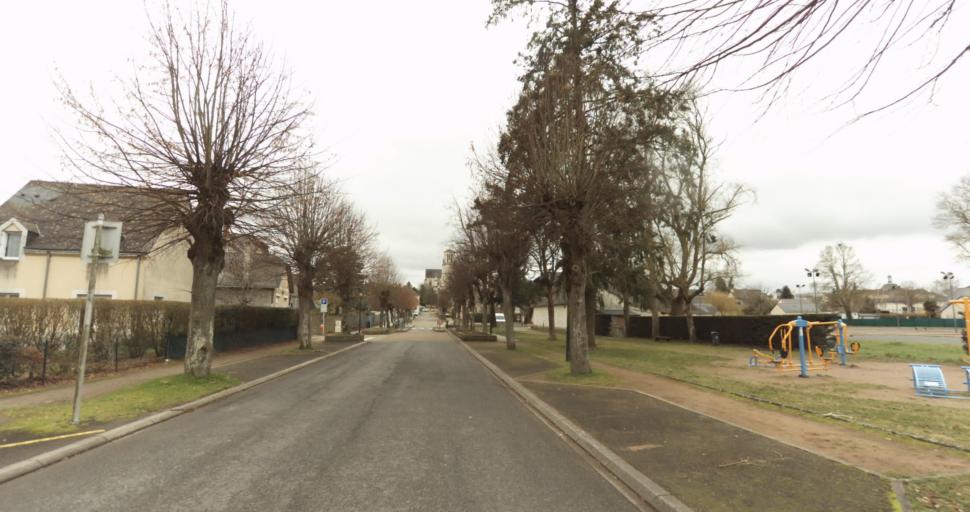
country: FR
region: Pays de la Loire
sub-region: Departement de Maine-et-Loire
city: Jumelles
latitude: 47.3812
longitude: -0.1151
